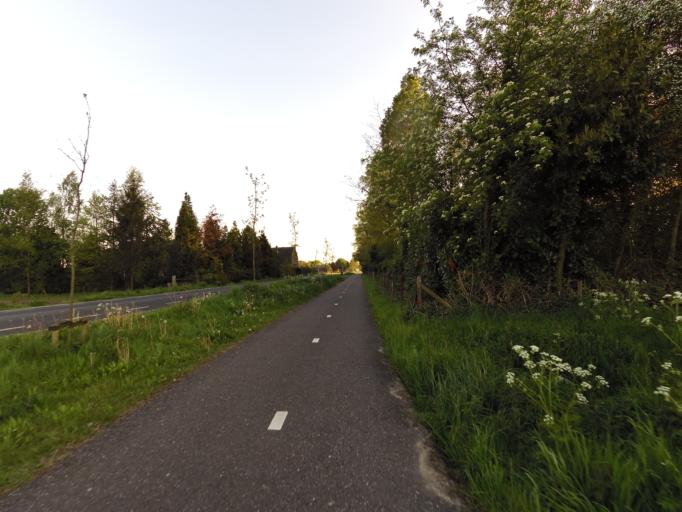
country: NL
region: Gelderland
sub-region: Oude IJsselstreek
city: Varsseveld
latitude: 51.9092
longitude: 6.4641
